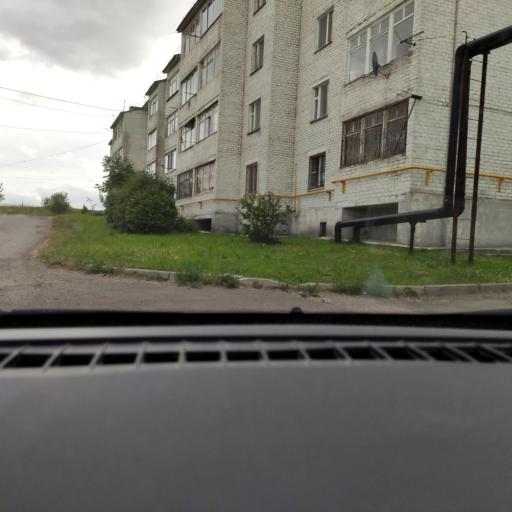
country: RU
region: Perm
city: Lobanovo
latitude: 57.8604
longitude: 56.2945
